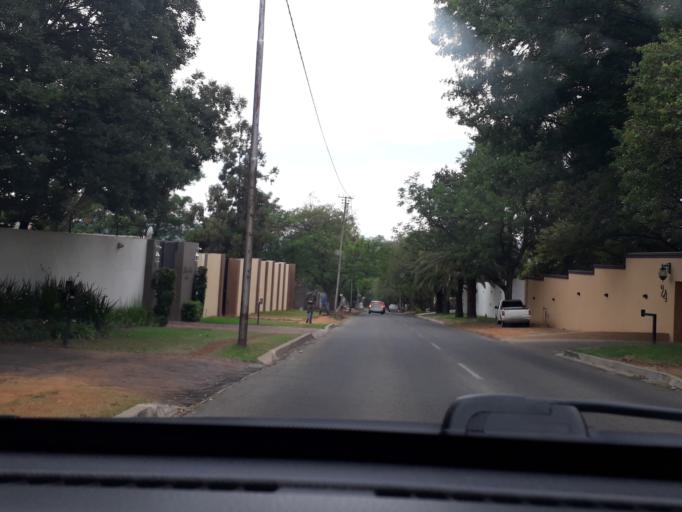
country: ZA
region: Gauteng
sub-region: City of Johannesburg Metropolitan Municipality
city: Johannesburg
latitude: -26.0747
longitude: 28.0229
